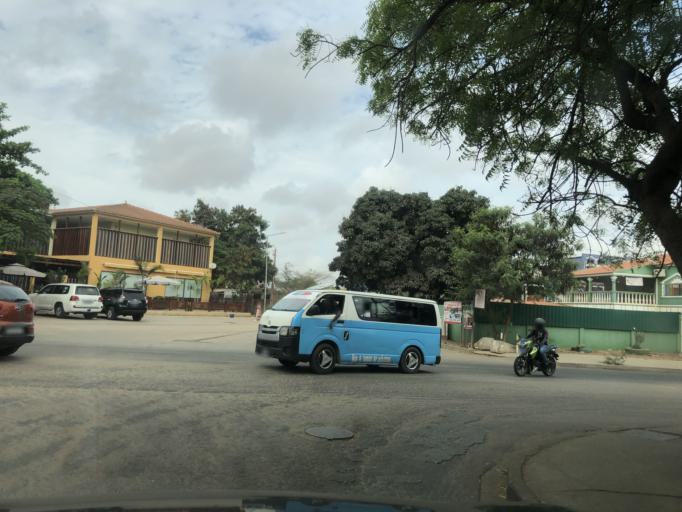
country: AO
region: Luanda
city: Luanda
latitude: -8.9186
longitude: 13.3733
